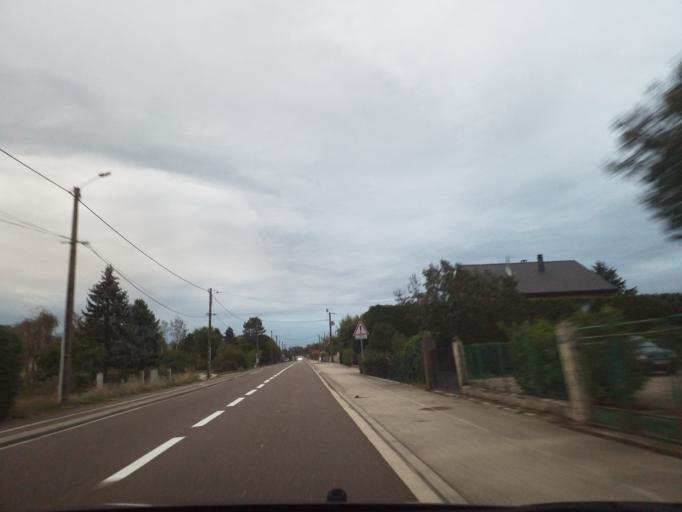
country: FR
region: Franche-Comte
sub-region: Departement de la Haute-Saone
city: Saint-Germain
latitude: 47.7287
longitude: 6.5401
